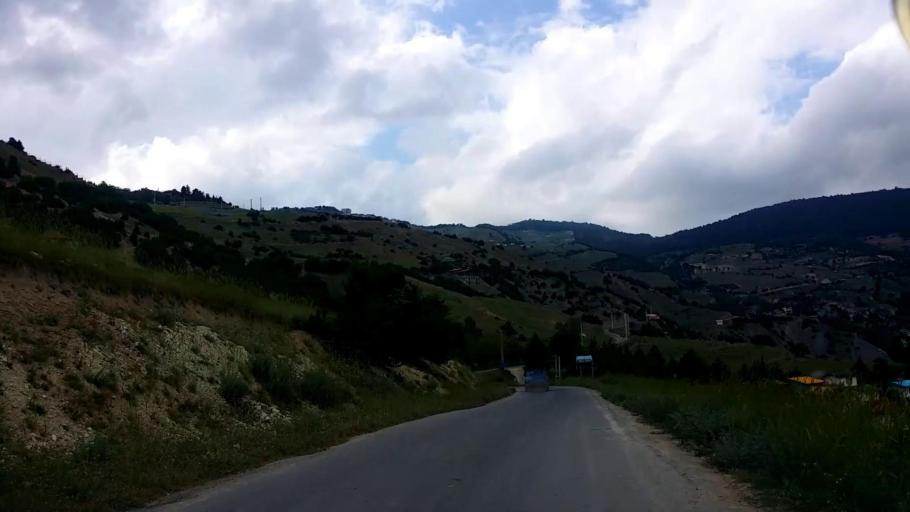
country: IR
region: Mazandaran
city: Chalus
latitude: 36.5427
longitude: 51.2720
